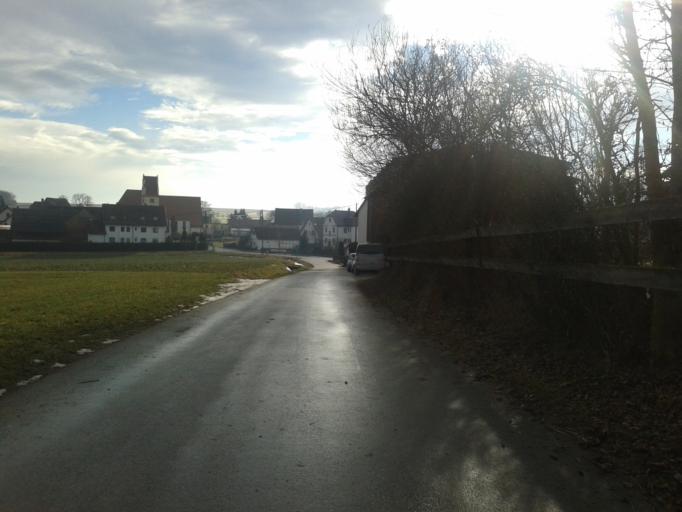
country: DE
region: Baden-Wuerttemberg
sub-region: Tuebingen Region
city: Erbach
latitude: 48.3557
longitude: 9.8953
